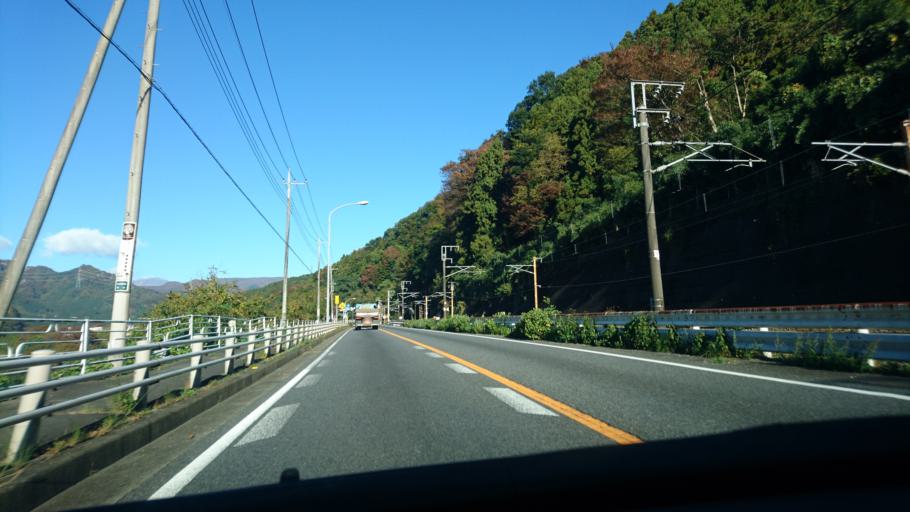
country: JP
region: Gunma
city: Annaka
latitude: 36.3321
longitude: 138.7505
